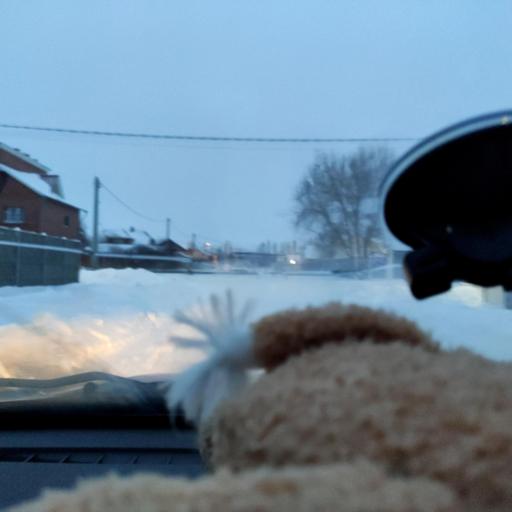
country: RU
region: Samara
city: Podstepki
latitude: 53.5102
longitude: 49.1720
